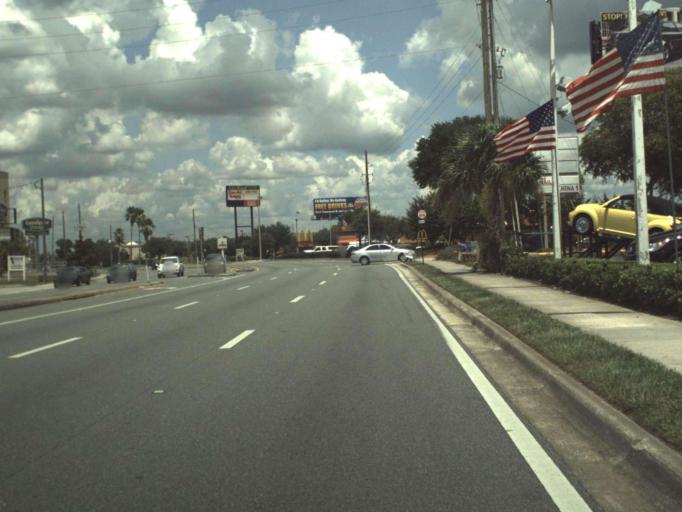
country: US
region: Florida
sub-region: Orange County
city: Fairview Shores
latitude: 28.6057
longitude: -81.3966
